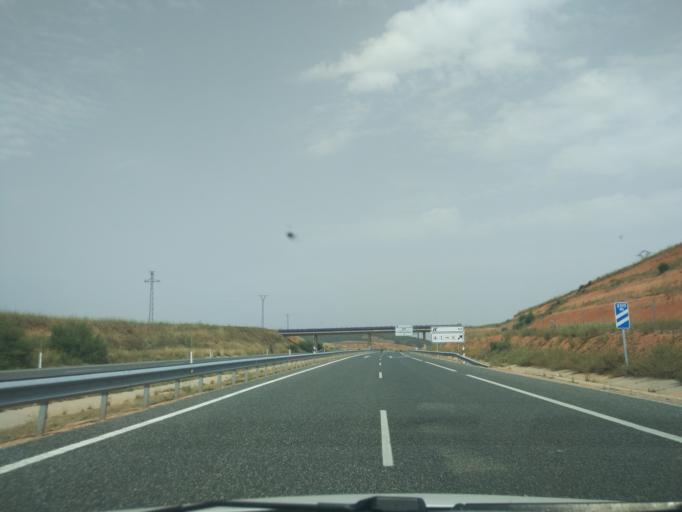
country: ES
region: Castille and Leon
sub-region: Provincia de Palencia
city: Alar del Rey
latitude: 42.6692
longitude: -4.3279
